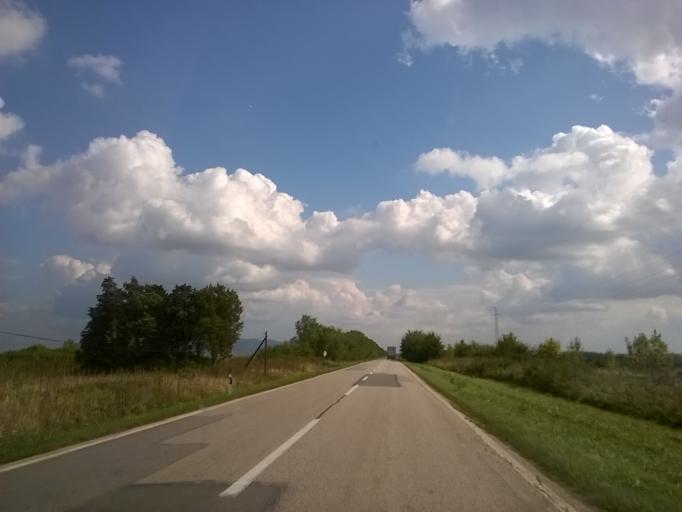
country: RS
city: Margita
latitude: 45.1810
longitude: 21.2102
